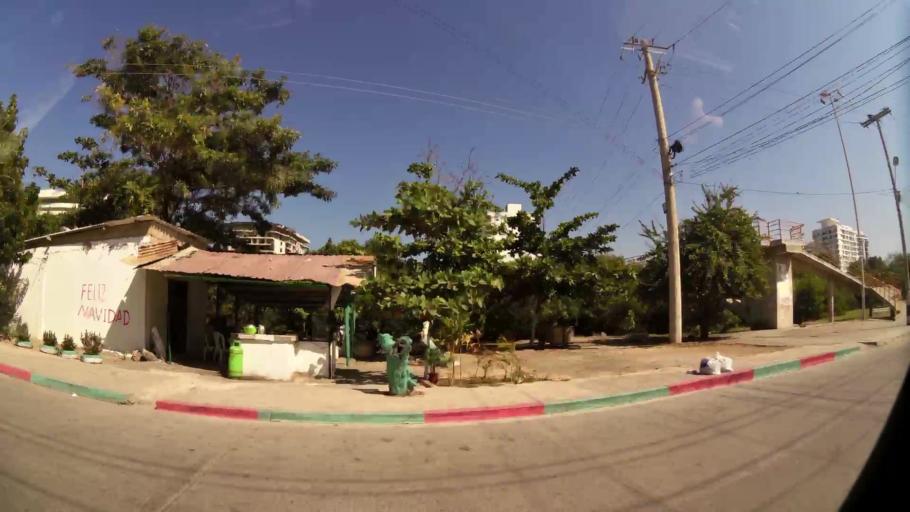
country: CO
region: Bolivar
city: Cartagena
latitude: 10.4418
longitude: -75.5240
